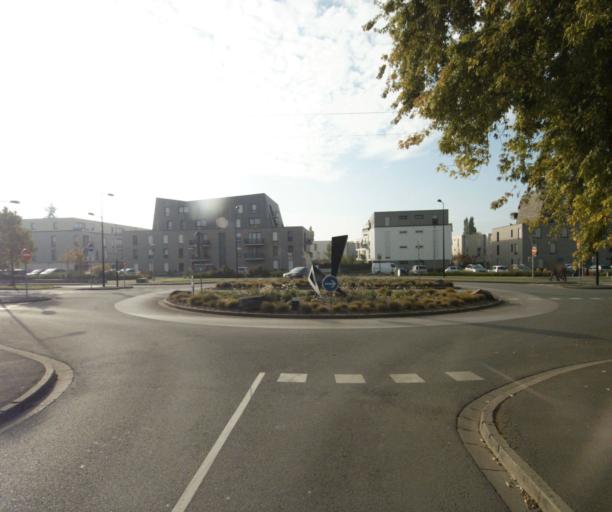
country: FR
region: Nord-Pas-de-Calais
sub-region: Departement du Nord
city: Wattignies
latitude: 50.5893
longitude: 3.0482
